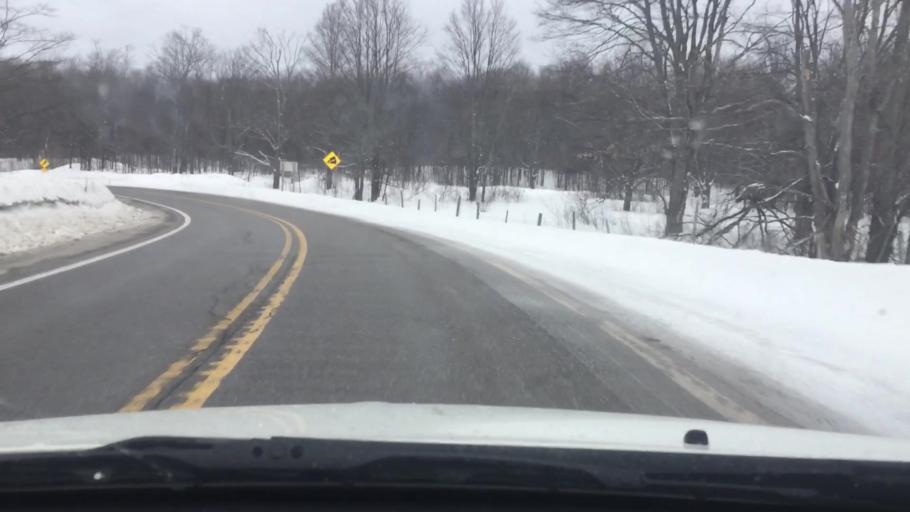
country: US
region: Michigan
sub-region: Charlevoix County
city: Boyne City
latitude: 45.0781
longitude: -84.9085
